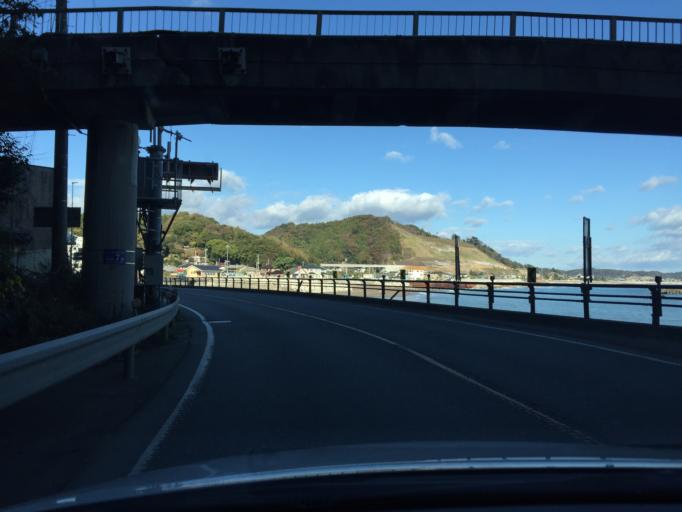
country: JP
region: Fukushima
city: Iwaki
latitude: 37.1177
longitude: 140.9992
